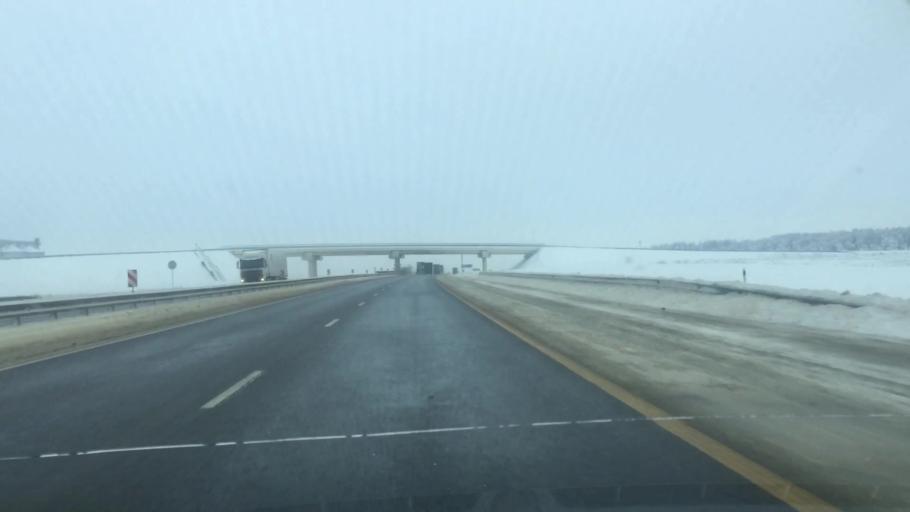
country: RU
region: Lipetsk
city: Stanovoye
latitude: 52.7445
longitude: 38.4683
